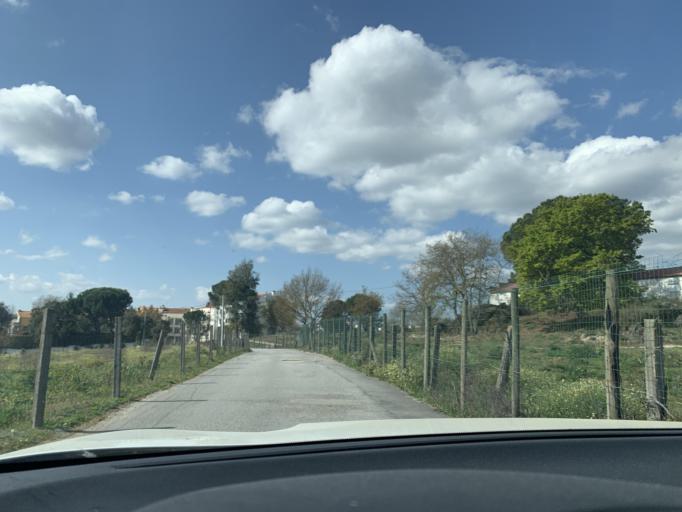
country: PT
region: Viseu
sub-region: Viseu
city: Rio de Loba
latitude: 40.6520
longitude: -7.8821
